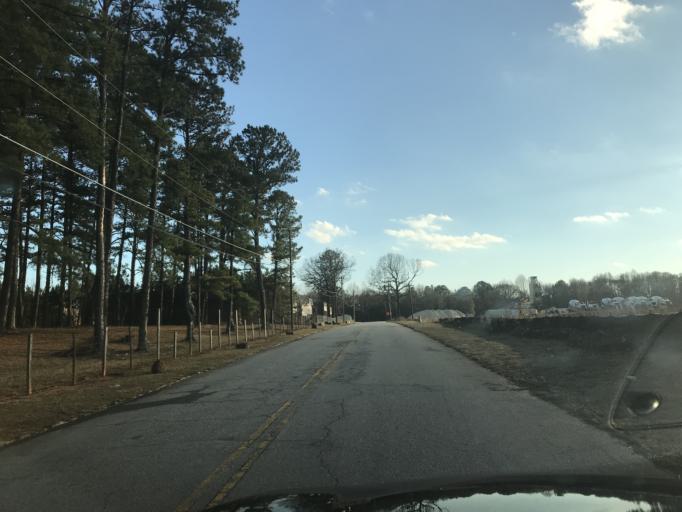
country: US
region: Georgia
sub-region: Fulton County
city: College Park
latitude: 33.6259
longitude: -84.4841
